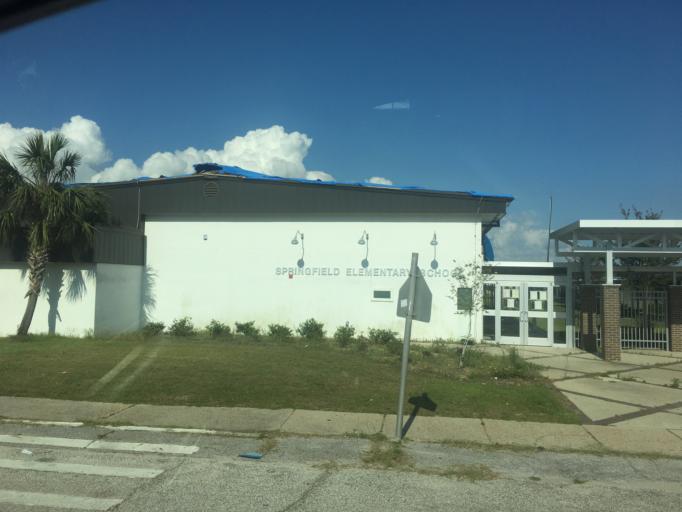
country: US
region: Florida
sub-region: Bay County
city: Springfield
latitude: 30.1575
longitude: -85.6165
